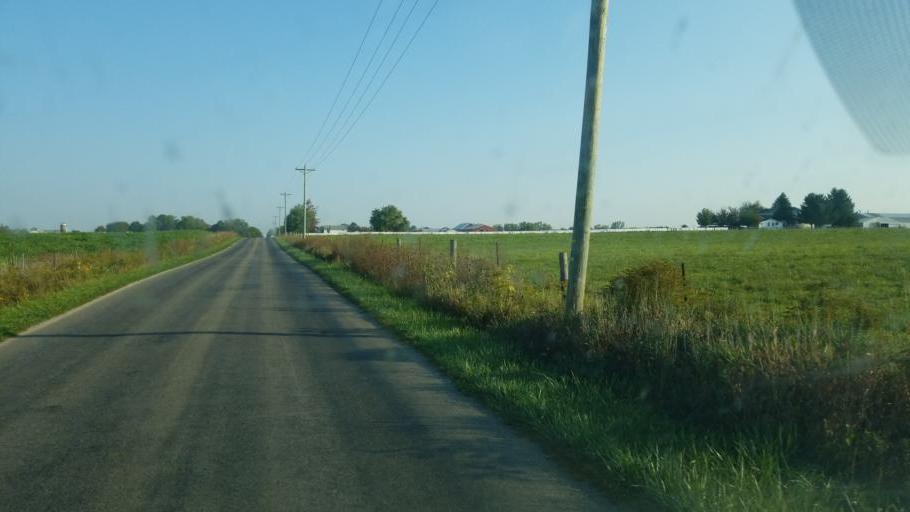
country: US
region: Indiana
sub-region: LaGrange County
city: Lagrange
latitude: 41.5853
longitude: -85.4240
